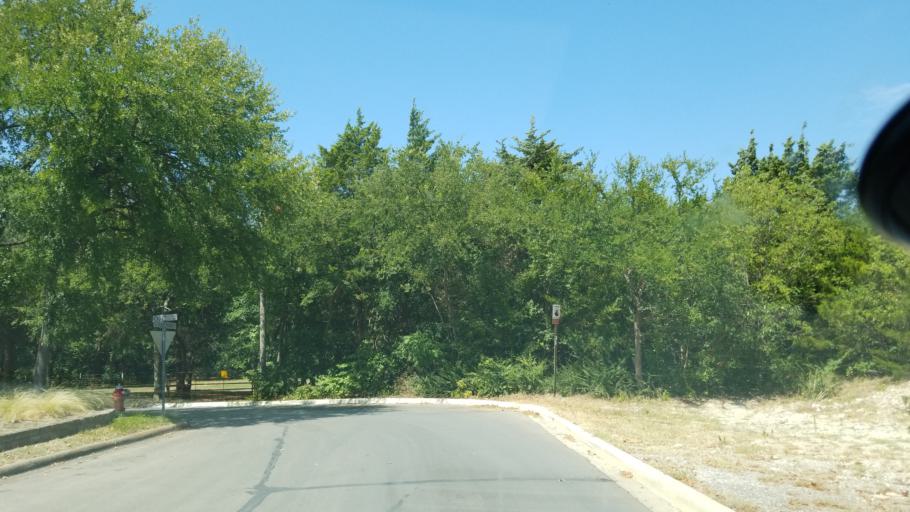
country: US
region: Texas
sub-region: Dallas County
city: Cockrell Hill
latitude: 32.7350
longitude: -96.8973
